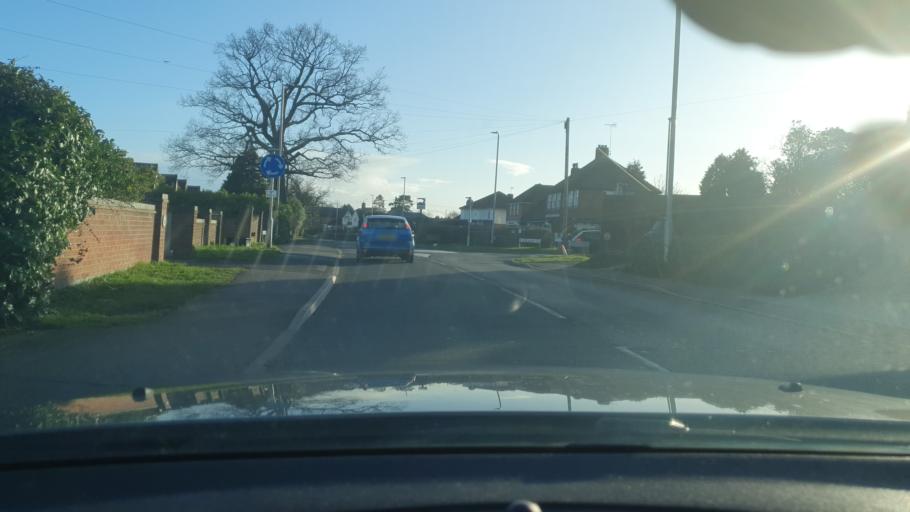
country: GB
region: England
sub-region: Wokingham
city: Woodley
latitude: 51.4467
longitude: -0.8988
